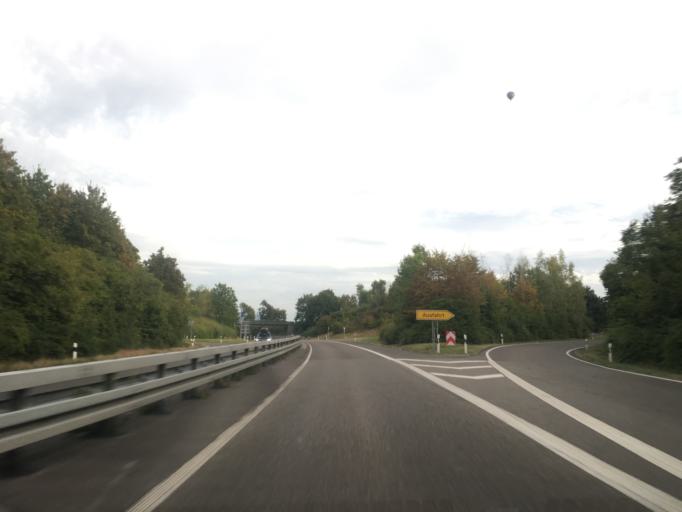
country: DE
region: Baden-Wuerttemberg
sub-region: Regierungsbezirk Stuttgart
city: Schlaitdorf
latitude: 48.6297
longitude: 9.2335
